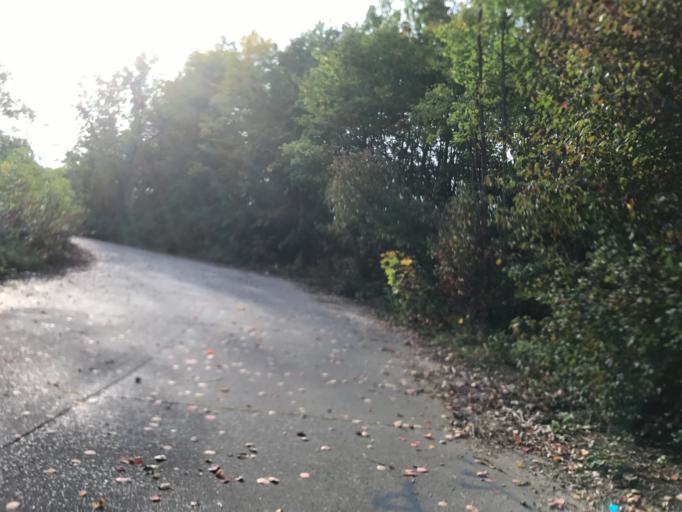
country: DE
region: Rheinland-Pfalz
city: Budenheim
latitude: 50.0114
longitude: 8.2123
